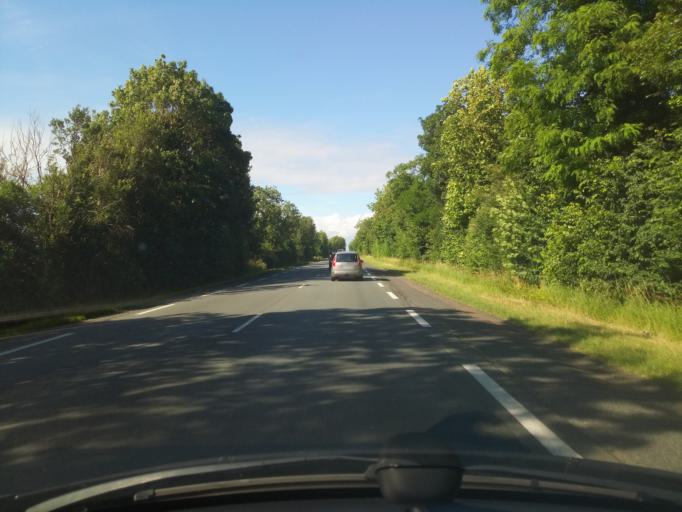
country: FR
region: Poitou-Charentes
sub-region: Departement de la Charente-Maritime
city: Andilly
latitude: 46.2709
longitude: -1.0036
